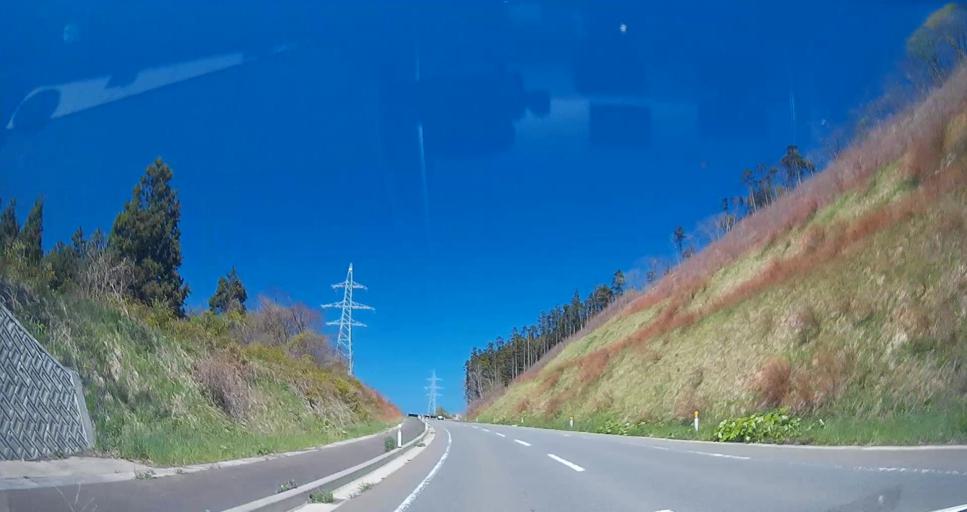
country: JP
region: Aomori
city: Mutsu
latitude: 41.3863
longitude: 141.4108
